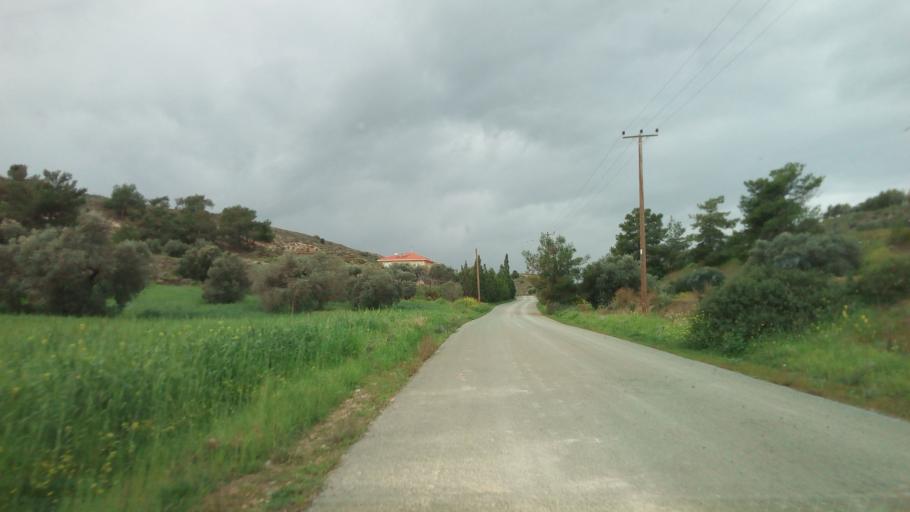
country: CY
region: Larnaka
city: Kofinou
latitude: 34.8578
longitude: 33.4492
